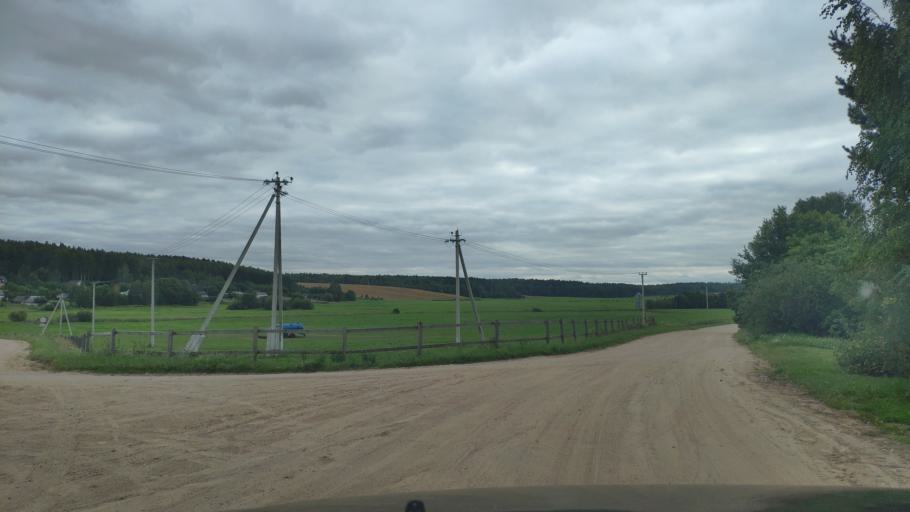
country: BY
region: Minsk
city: Khatsyezhyna
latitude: 53.9309
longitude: 27.2670
